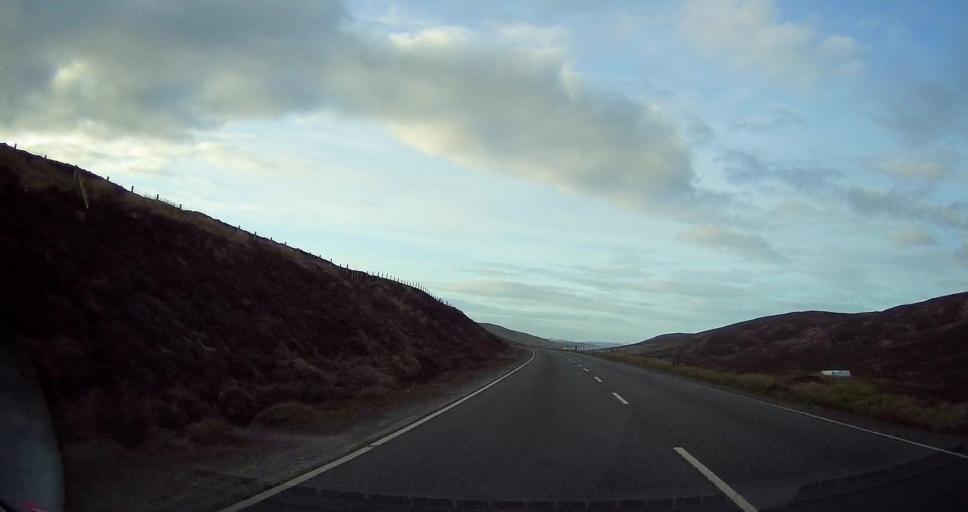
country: GB
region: Scotland
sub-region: Shetland Islands
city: Lerwick
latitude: 60.1466
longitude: -1.2406
